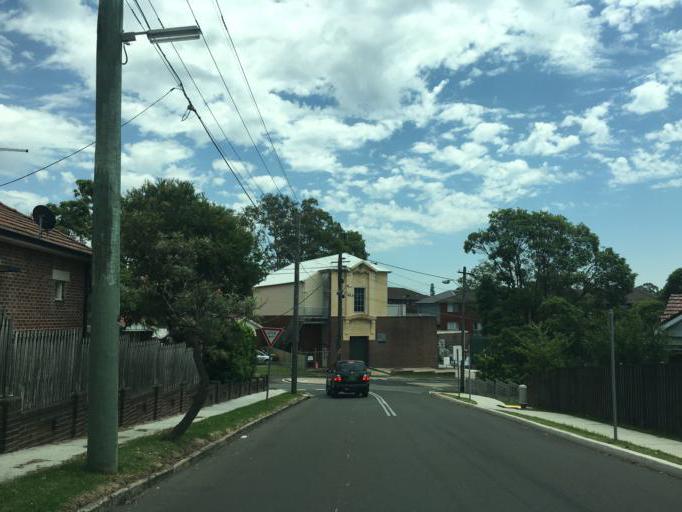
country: AU
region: New South Wales
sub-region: Hunters Hill
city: Gladesville
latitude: -33.8289
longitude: 151.1296
